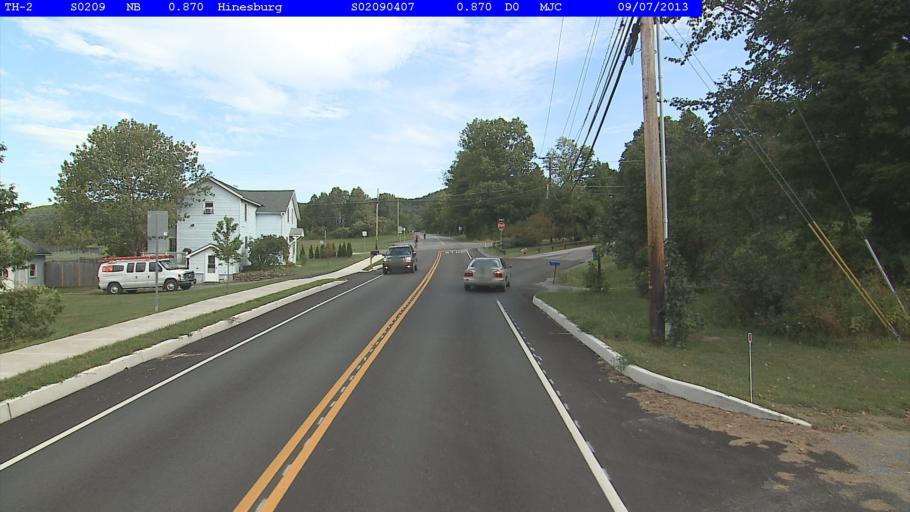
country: US
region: Vermont
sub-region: Chittenden County
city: Hinesburg
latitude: 44.3429
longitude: -73.1056
